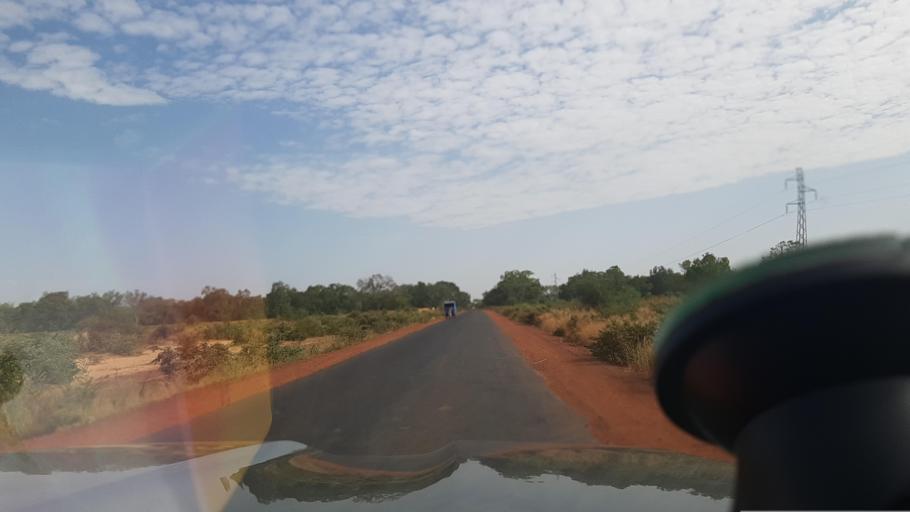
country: ML
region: Segou
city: Segou
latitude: 13.5258
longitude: -6.1308
